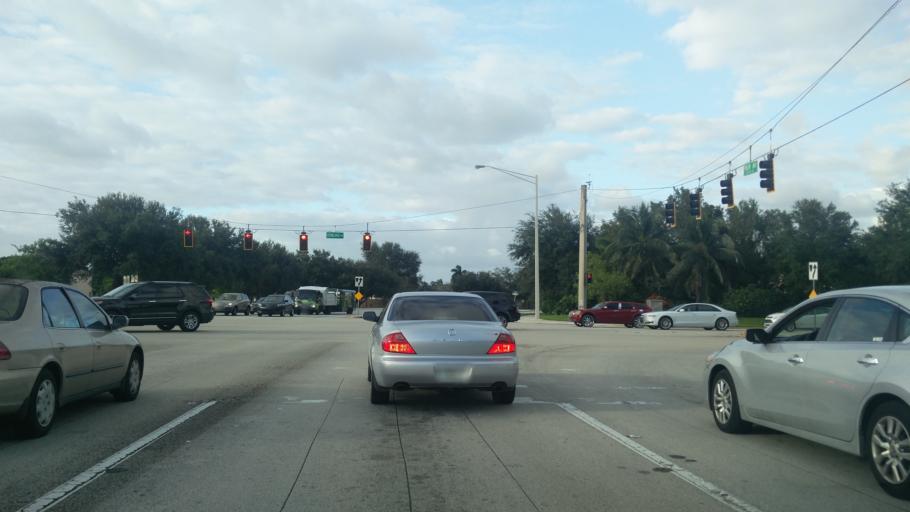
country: US
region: Florida
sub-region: Broward County
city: Cooper City
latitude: 26.0442
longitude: -80.2809
